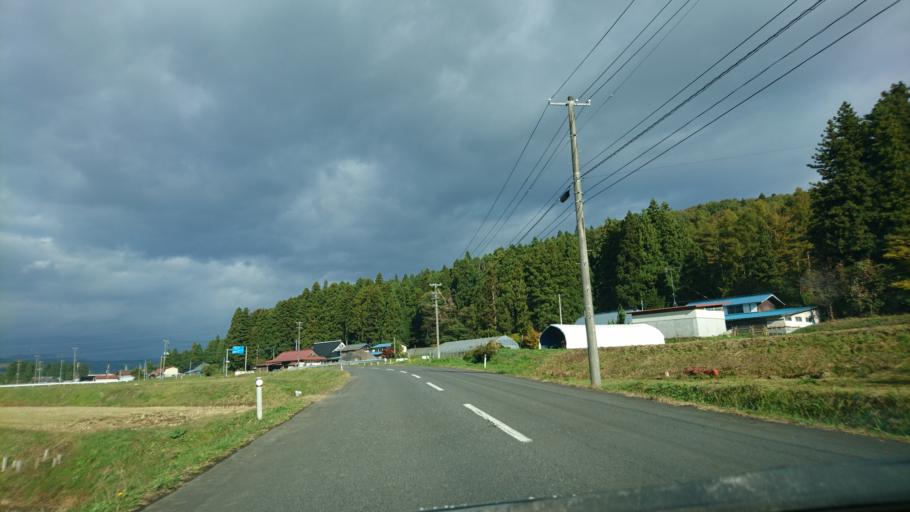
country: JP
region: Iwate
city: Mizusawa
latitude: 39.0748
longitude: 141.0128
